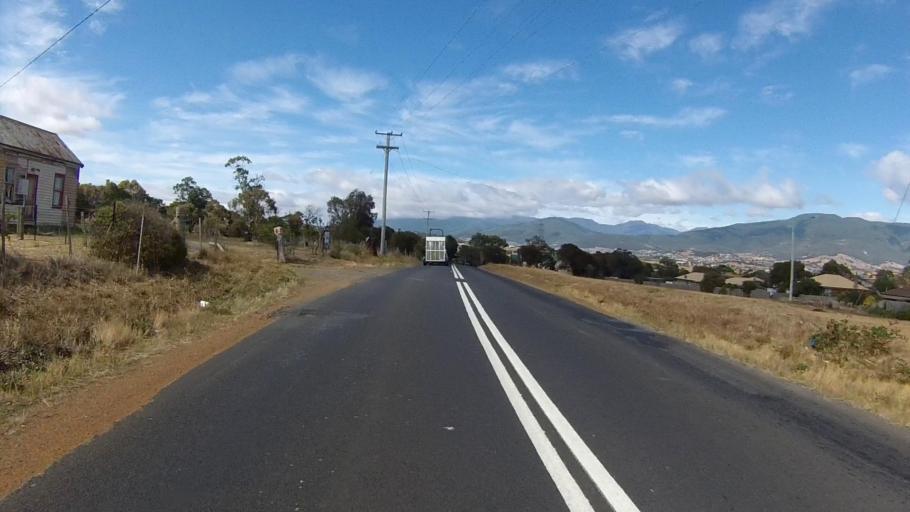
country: AU
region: Tasmania
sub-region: Brighton
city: Old Beach
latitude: -42.7484
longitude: 147.2806
